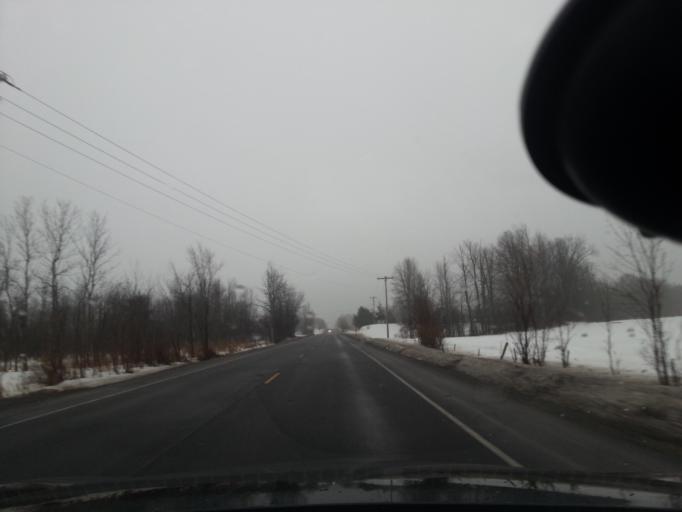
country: US
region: New York
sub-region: St. Lawrence County
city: Ogdensburg
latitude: 44.6047
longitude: -75.3916
